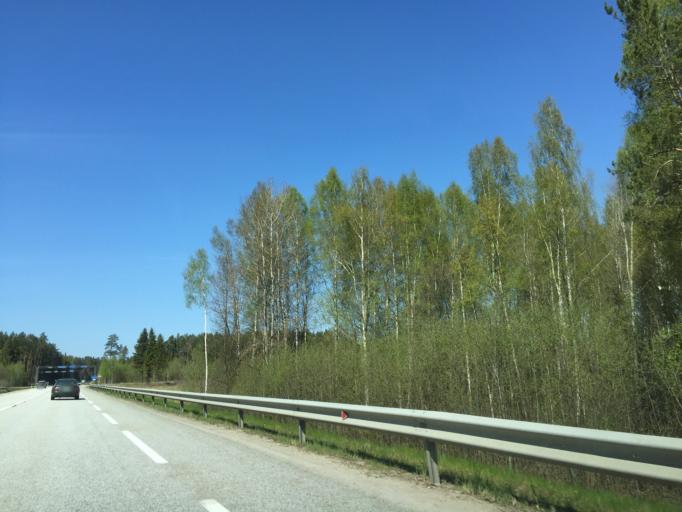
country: LV
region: Saulkrastu
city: Saulkrasti
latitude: 57.3407
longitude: 24.4475
